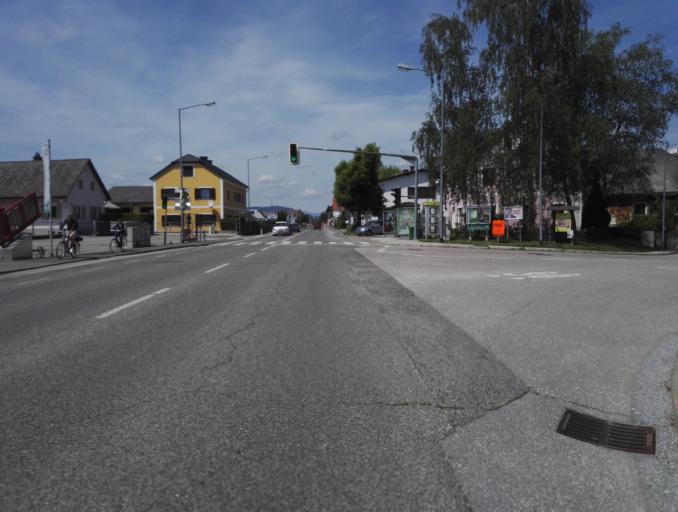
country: AT
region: Styria
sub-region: Politischer Bezirk Graz-Umgebung
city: Feldkirchen bei Graz
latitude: 46.9959
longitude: 15.4533
